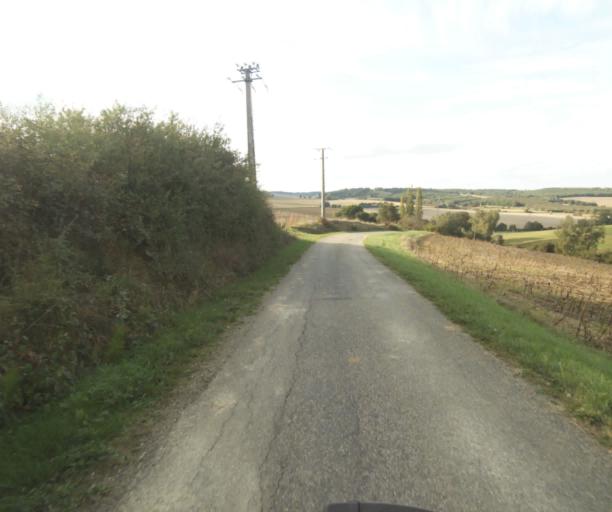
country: FR
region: Midi-Pyrenees
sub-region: Departement de la Haute-Garonne
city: Launac
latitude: 43.8167
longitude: 1.0922
